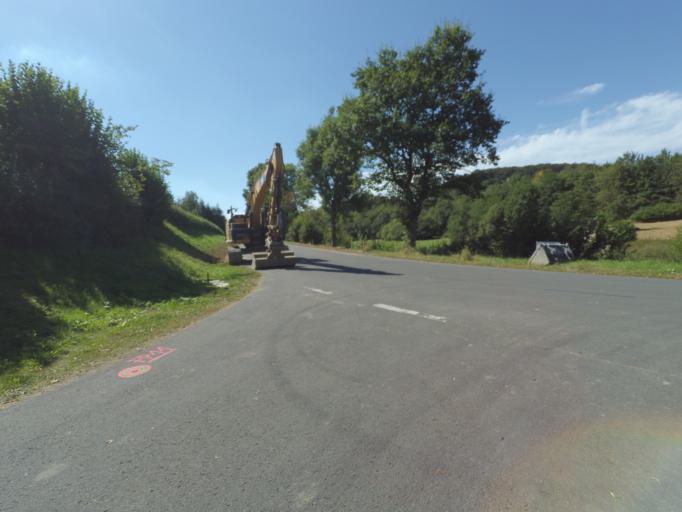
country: DE
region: Rheinland-Pfalz
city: Steiningen
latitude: 50.1872
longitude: 6.9096
